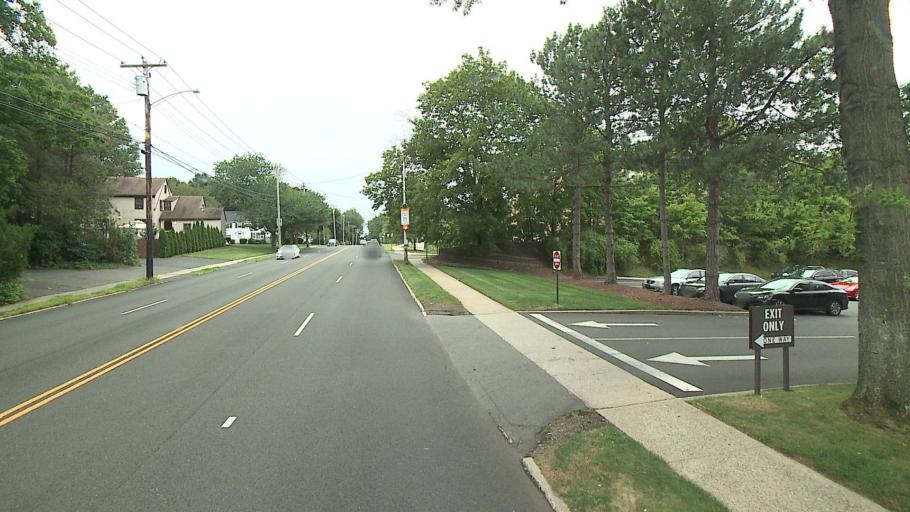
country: US
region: Connecticut
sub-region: New Haven County
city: Hamden
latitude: 41.3695
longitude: -72.9069
